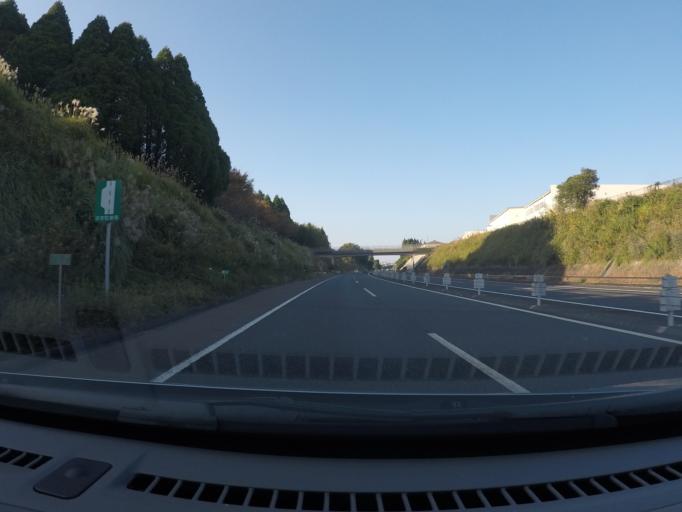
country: JP
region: Kagoshima
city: Kajiki
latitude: 31.8068
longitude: 130.7085
